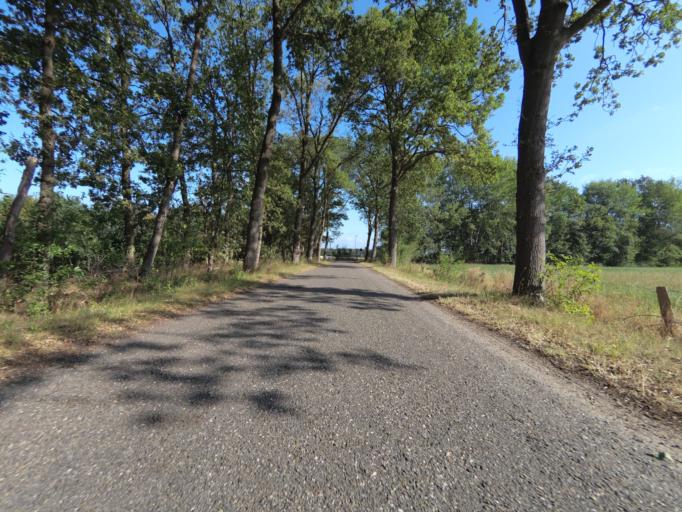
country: NL
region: Overijssel
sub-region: Gemeente Oldenzaal
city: Oldenzaal
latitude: 52.2797
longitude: 6.9055
